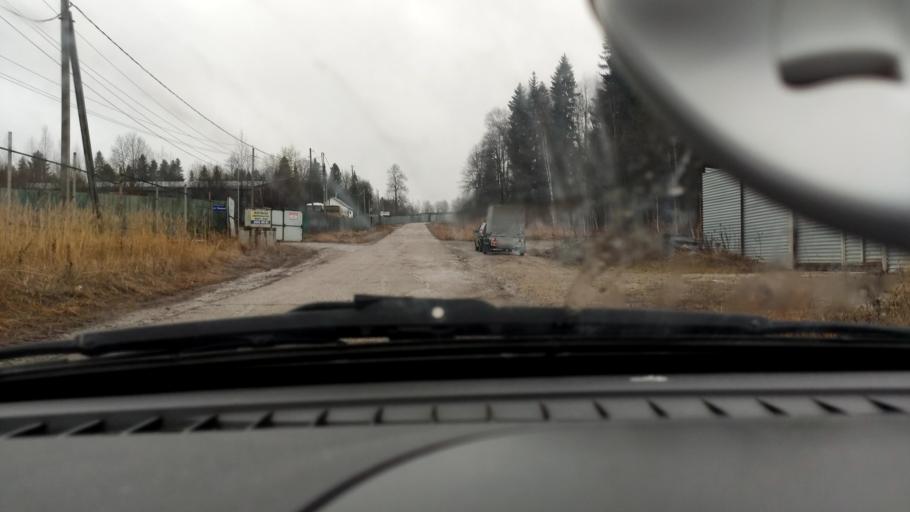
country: RU
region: Perm
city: Perm
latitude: 58.0329
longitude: 56.4129
